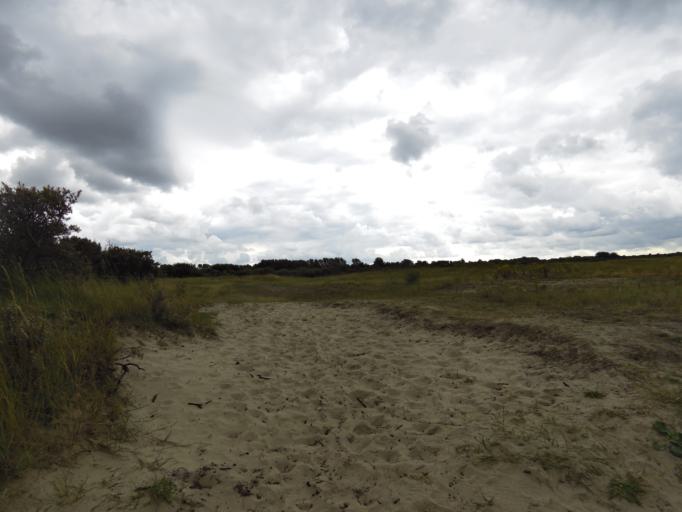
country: NL
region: South Holland
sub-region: Gemeente Goeree-Overflakkee
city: Goedereede
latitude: 51.8402
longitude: 3.9838
